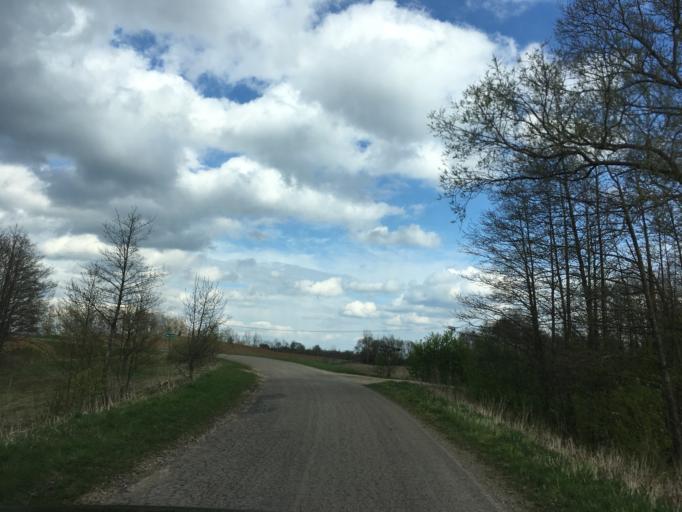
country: PL
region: Podlasie
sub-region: Suwalki
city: Suwalki
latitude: 54.3686
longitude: 22.9222
